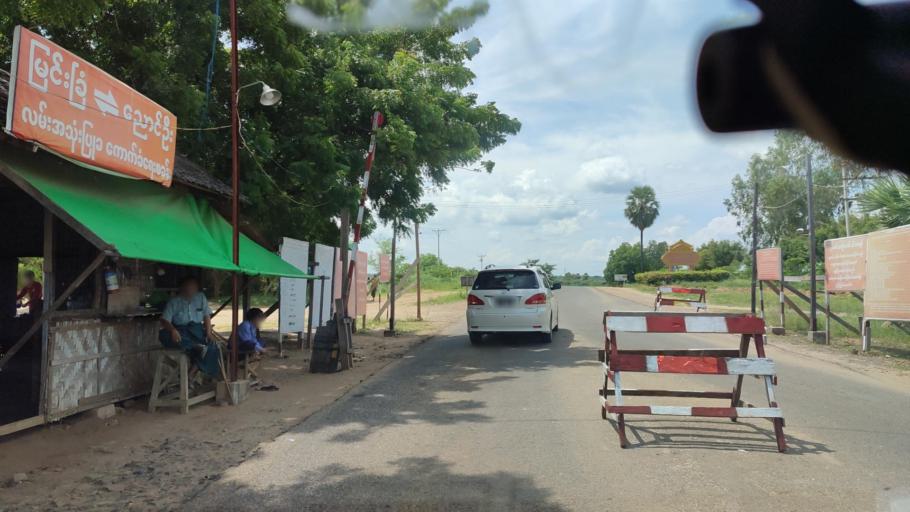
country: MM
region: Magway
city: Pakokku
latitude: 21.1980
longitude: 94.9603
